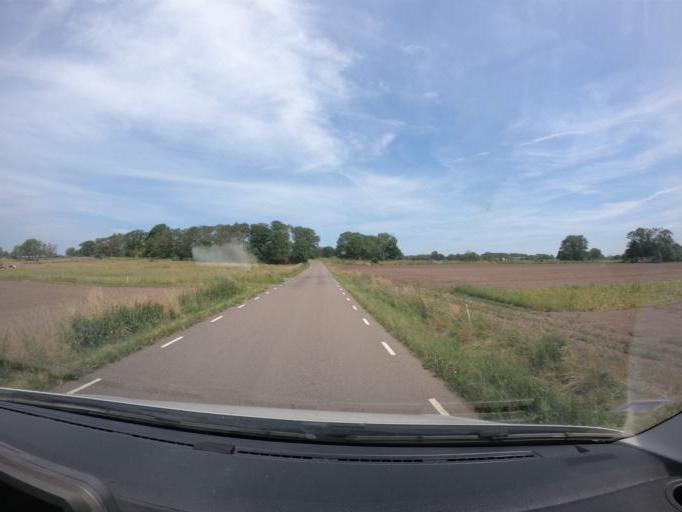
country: SE
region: Skane
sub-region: Angelholms Kommun
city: Vejbystrand
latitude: 56.3812
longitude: 12.7039
